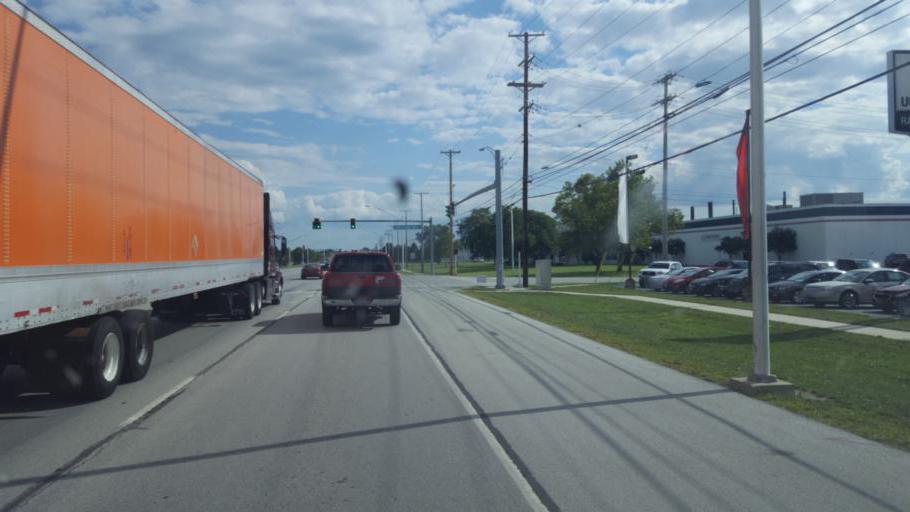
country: US
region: Ohio
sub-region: Wood County
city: Bowling Green
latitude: 41.3973
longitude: -83.6507
